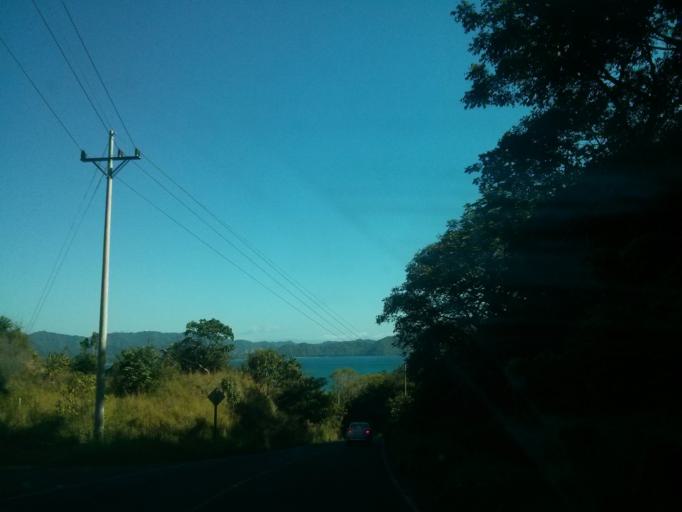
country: CR
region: Puntarenas
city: Paquera
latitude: 9.7113
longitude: -85.0155
